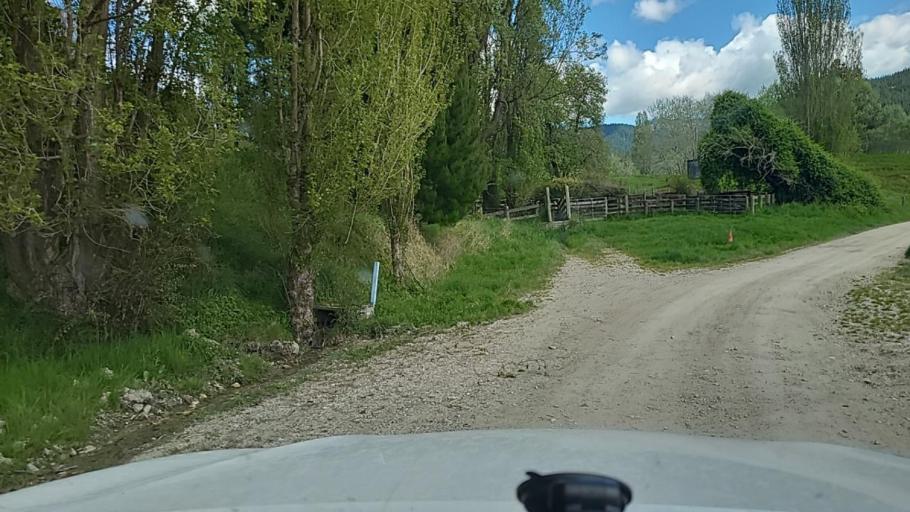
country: NZ
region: Gisborne
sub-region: Gisborne District
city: Gisborne
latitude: -38.7866
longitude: 177.7797
